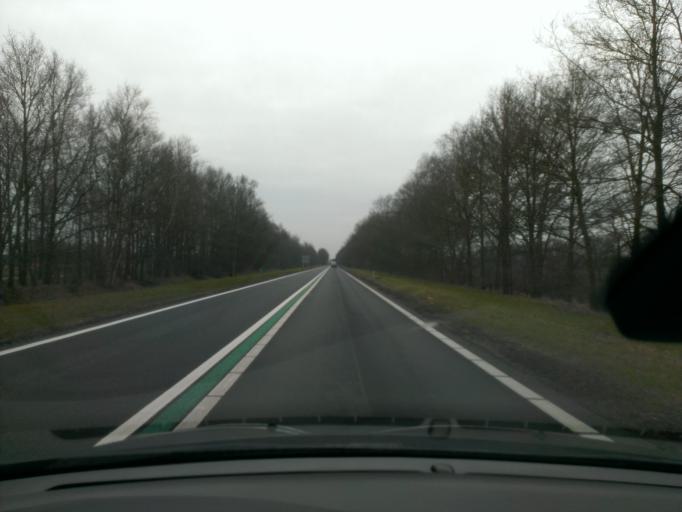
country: NL
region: Overijssel
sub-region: Gemeente Twenterand
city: Westerhaar-Vriezenveensewijk
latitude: 52.4594
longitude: 6.6265
